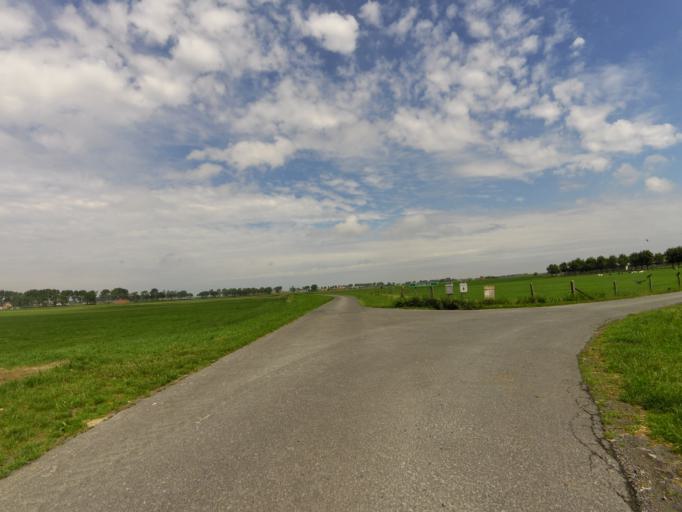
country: BE
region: Flanders
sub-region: Provincie West-Vlaanderen
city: Nieuwpoort
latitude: 51.1380
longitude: 2.7846
